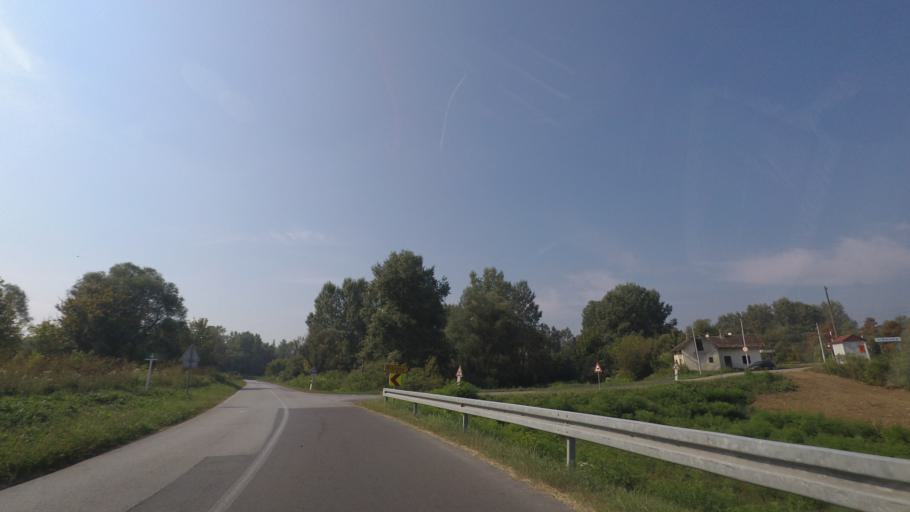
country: BA
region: Republika Srpska
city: Bosanska Dubica
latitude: 45.2568
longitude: 16.8814
